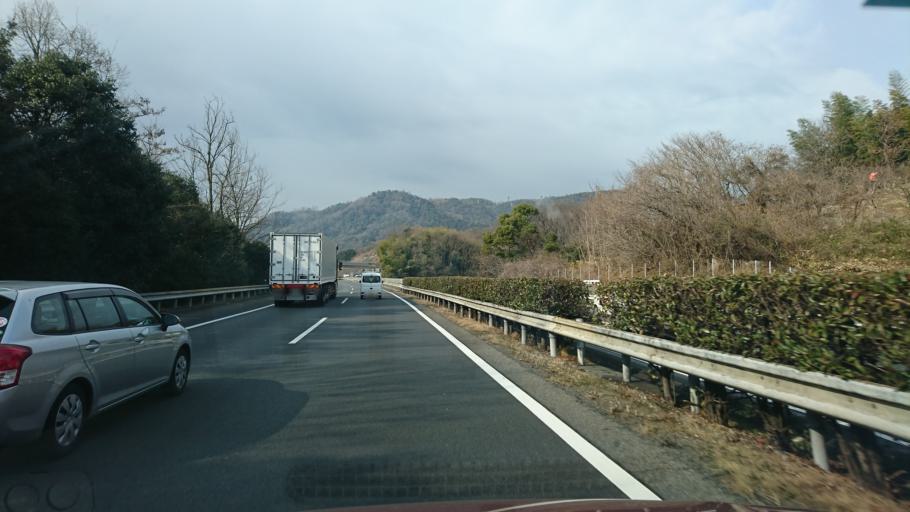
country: JP
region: Okayama
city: Kamogatacho-kamogata
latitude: 34.5684
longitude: 133.6357
